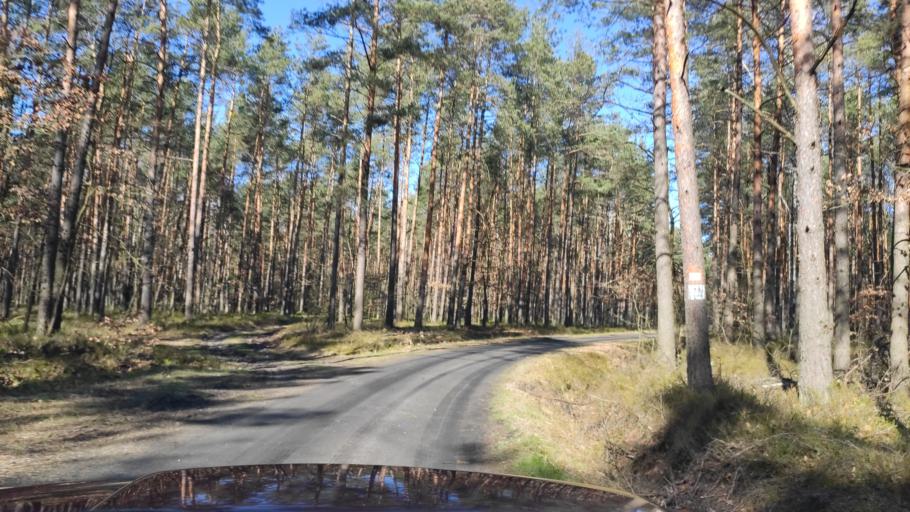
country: PL
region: Masovian Voivodeship
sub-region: Powiat zwolenski
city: Zwolen
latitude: 51.4092
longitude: 21.5575
